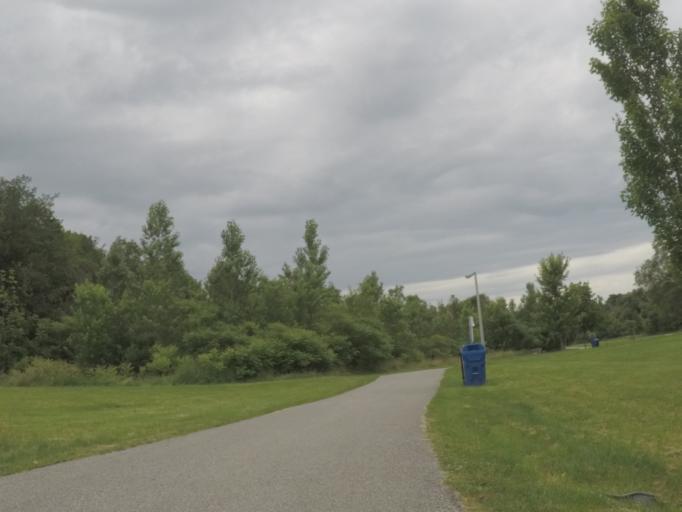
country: CA
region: Ontario
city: Etobicoke
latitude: 43.6663
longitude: -79.5667
